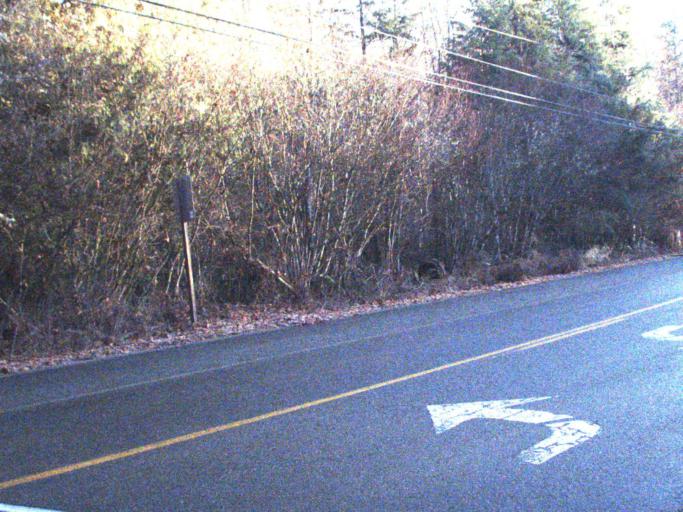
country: US
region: Washington
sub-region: Snohomish County
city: Darrington
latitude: 48.5267
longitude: -121.4351
